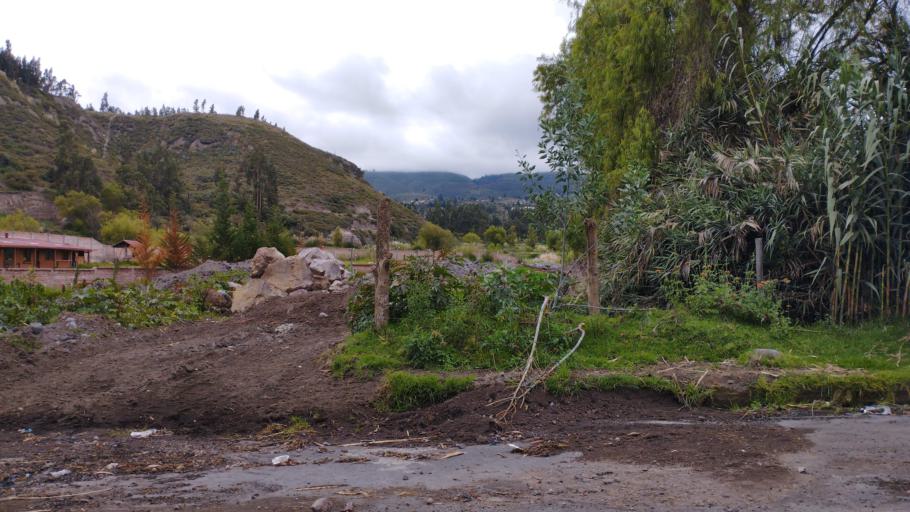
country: EC
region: Chimborazo
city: Guano
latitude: -1.6179
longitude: -78.6082
